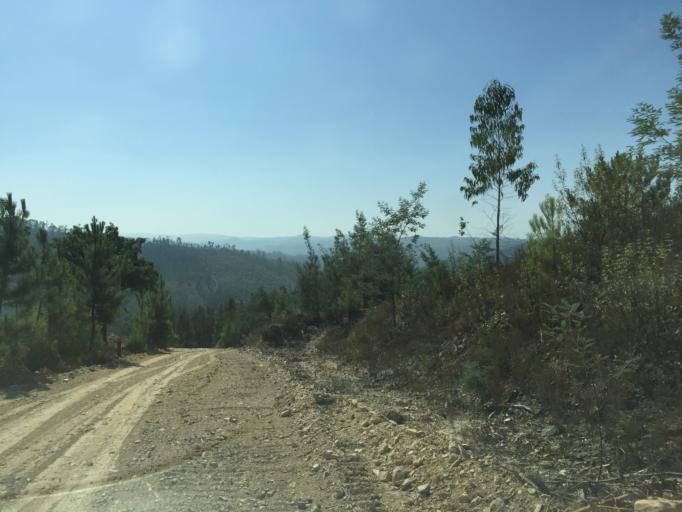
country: PT
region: Santarem
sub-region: Ferreira do Zezere
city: Ferreira do Zezere
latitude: 39.6549
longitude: -8.2393
